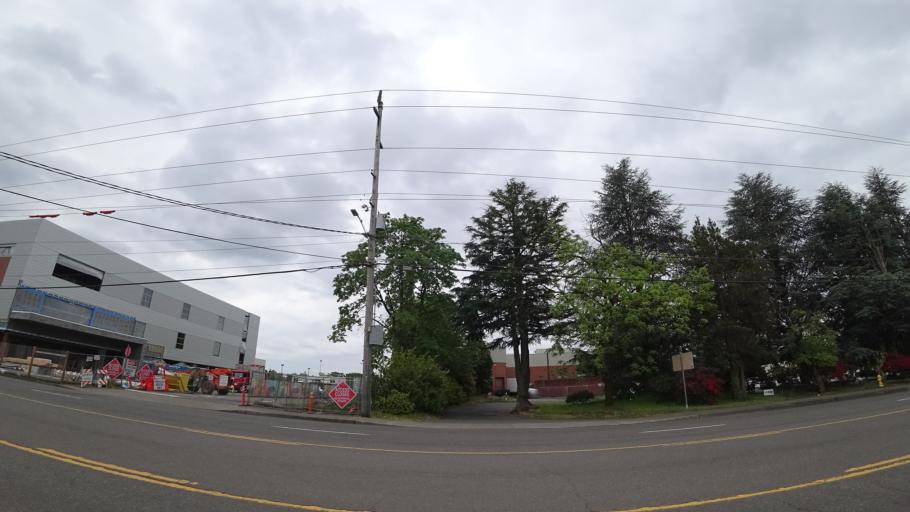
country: US
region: Oregon
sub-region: Washington County
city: Beaverton
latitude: 45.4866
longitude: -122.7846
